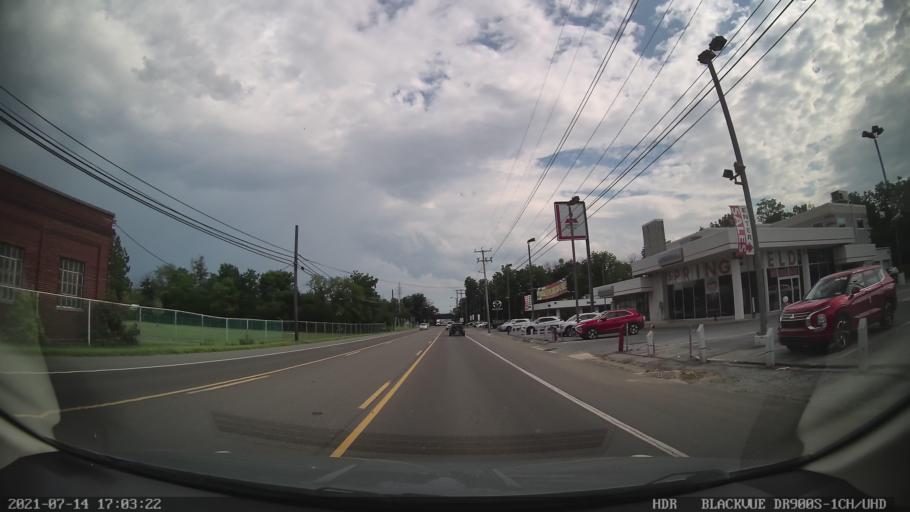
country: US
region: Pennsylvania
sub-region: Berks County
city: Muhlenberg Park
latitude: 40.3937
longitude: -75.9354
